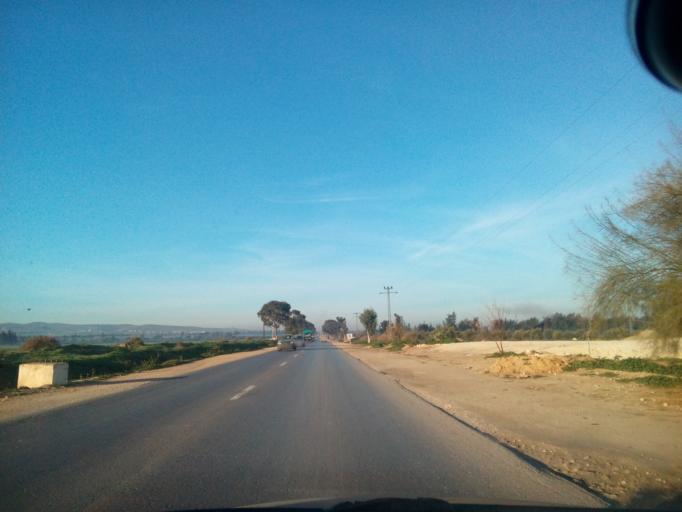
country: DZ
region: Relizane
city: Relizane
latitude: 35.7327
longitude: 0.4500
